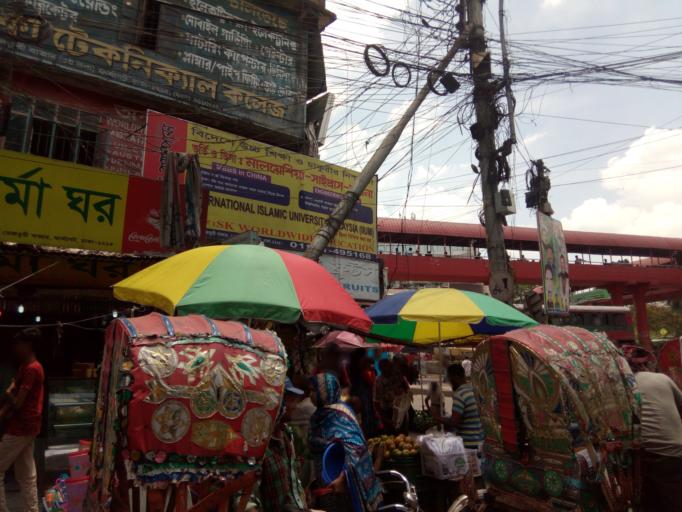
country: BD
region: Dhaka
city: Azimpur
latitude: 23.7583
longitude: 90.3906
